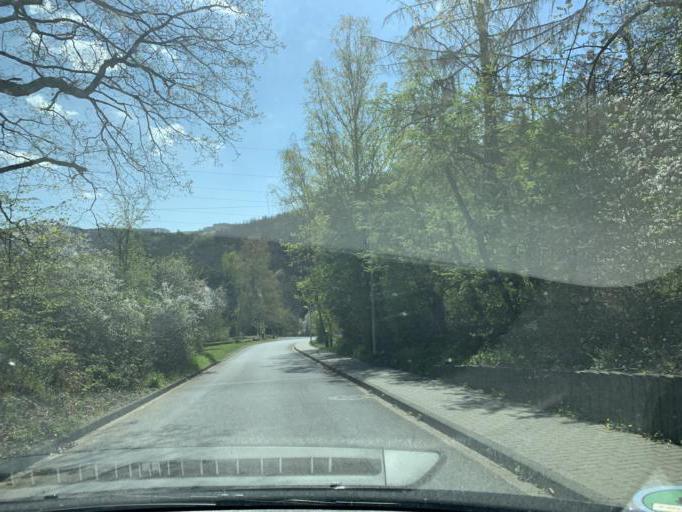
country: DE
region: North Rhine-Westphalia
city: Heimbach
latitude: 50.6315
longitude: 6.4560
